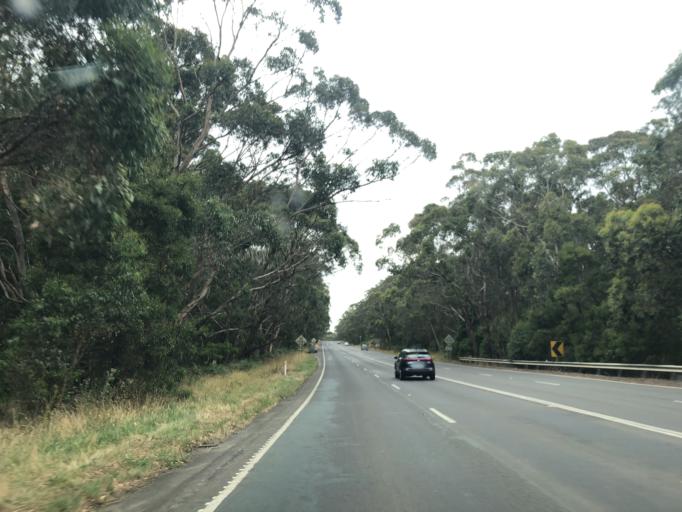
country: AU
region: Victoria
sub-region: Hume
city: Sunbury
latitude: -37.4004
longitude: 144.5303
